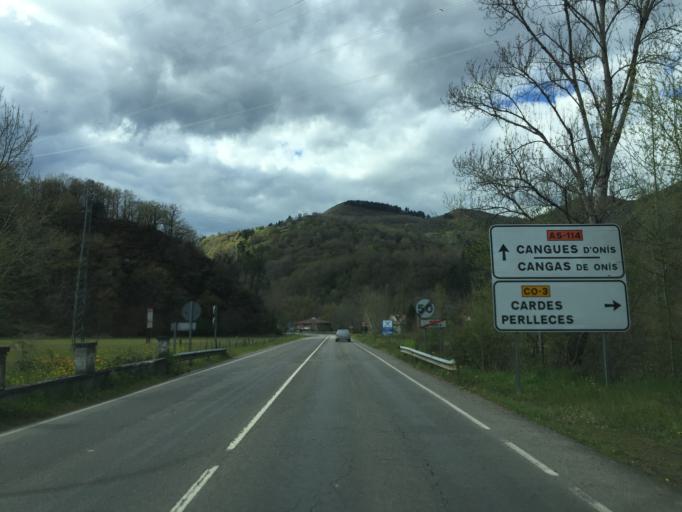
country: ES
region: Asturias
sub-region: Province of Asturias
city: Cangas de Onis
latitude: 43.3494
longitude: -5.0926
